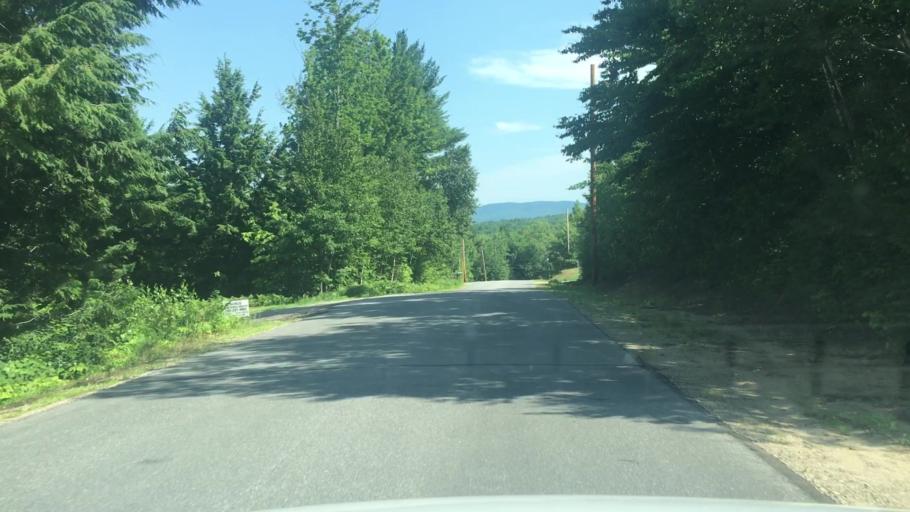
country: US
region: Maine
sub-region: Oxford County
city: West Paris
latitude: 44.3238
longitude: -70.5094
